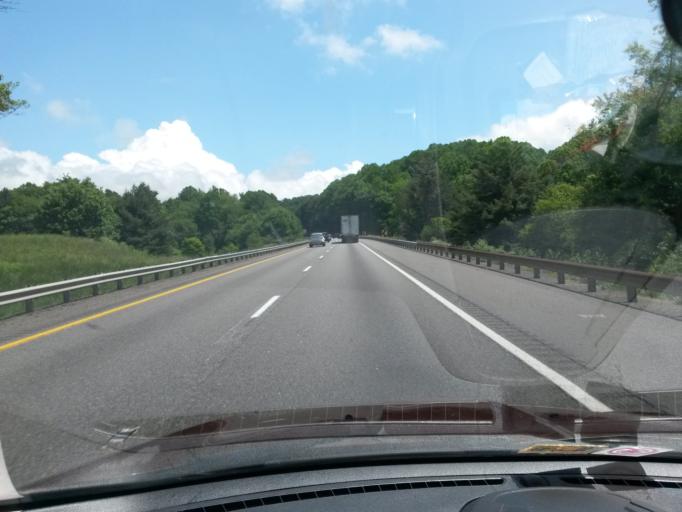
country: US
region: Virginia
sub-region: Carroll County
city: Hillsville
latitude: 36.7379
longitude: -80.7686
